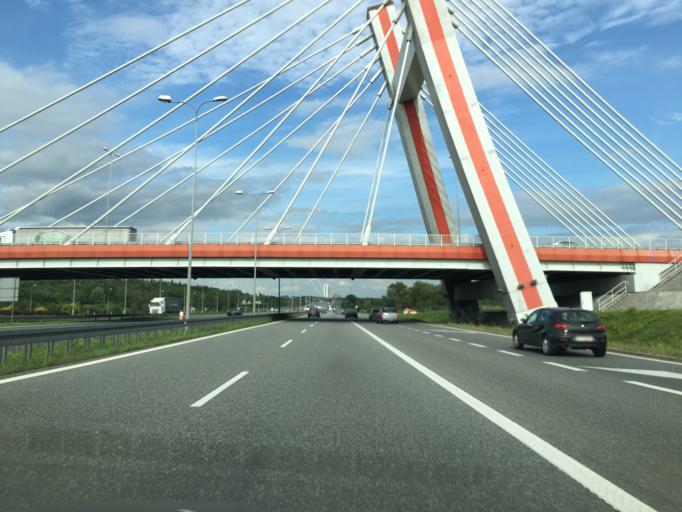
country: PL
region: Silesian Voivodeship
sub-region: Powiat gliwicki
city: Przyszowice
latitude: 50.2645
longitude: 18.7364
